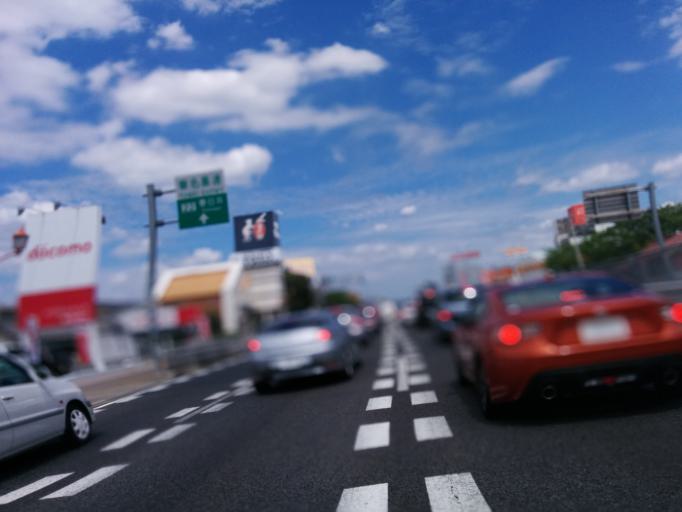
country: JP
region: Aichi
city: Kasugai
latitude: 35.2421
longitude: 136.9645
